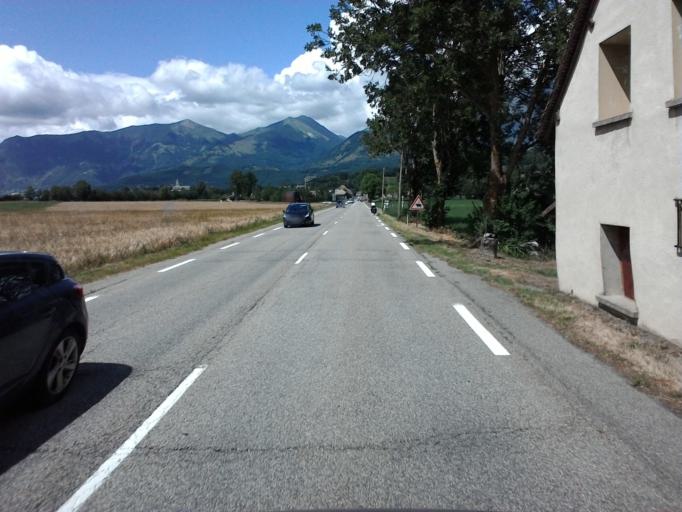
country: FR
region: Provence-Alpes-Cote d'Azur
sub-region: Departement des Hautes-Alpes
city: Saint-Bonnet-en-Champsaur
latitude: 44.7476
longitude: 6.0081
